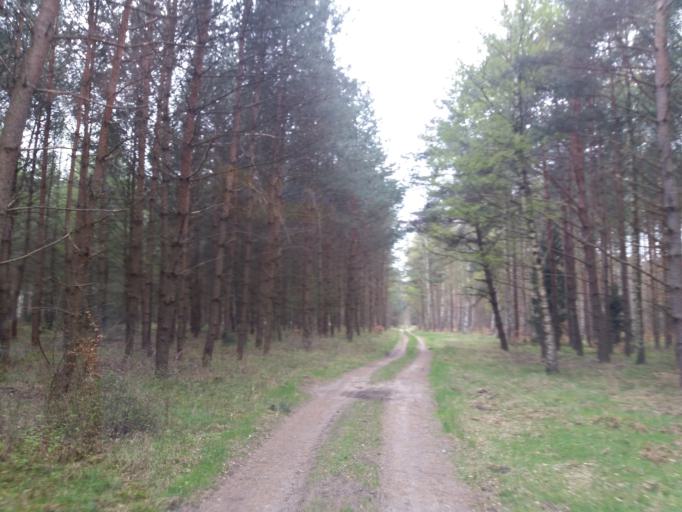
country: PL
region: Lubusz
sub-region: Powiat strzelecko-drezdenecki
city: Dobiegniew
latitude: 53.0856
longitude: 15.8177
